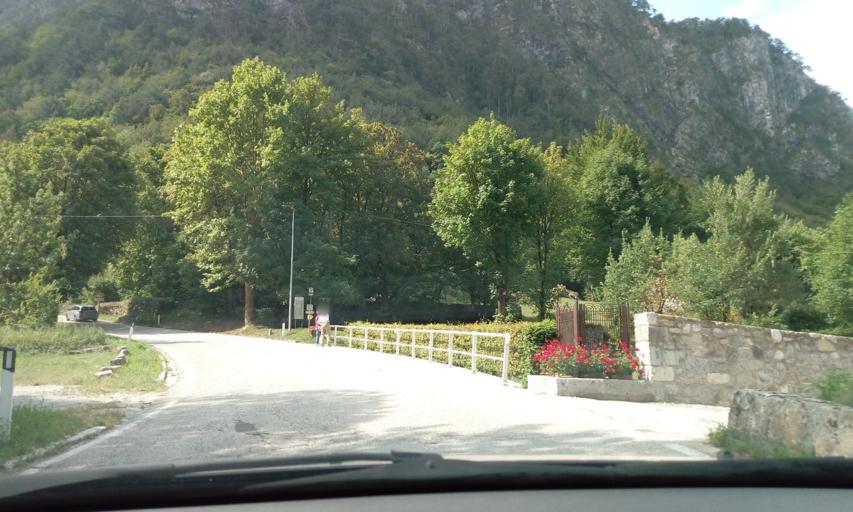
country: IT
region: Friuli Venezia Giulia
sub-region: Provincia di Udine
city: Chiusaforte
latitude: 46.4042
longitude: 13.3171
